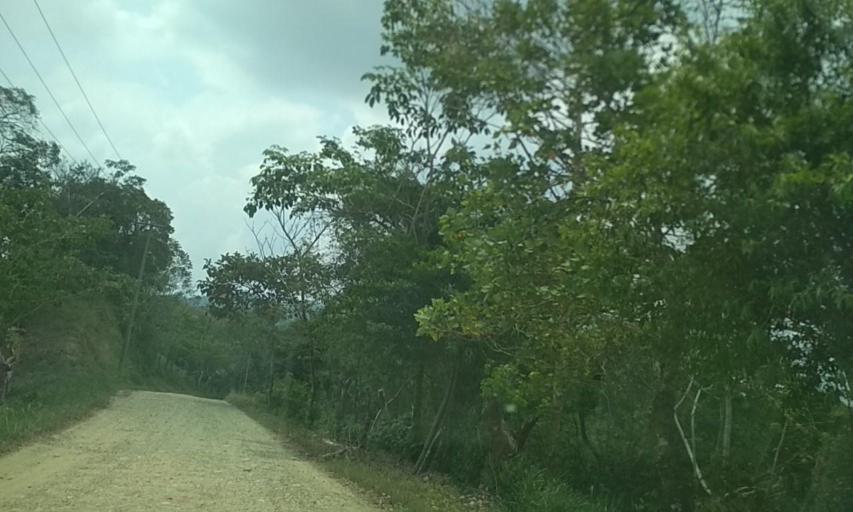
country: MX
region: Tabasco
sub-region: Huimanguillo
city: Francisco Rueda
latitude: 17.5894
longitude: -93.7932
